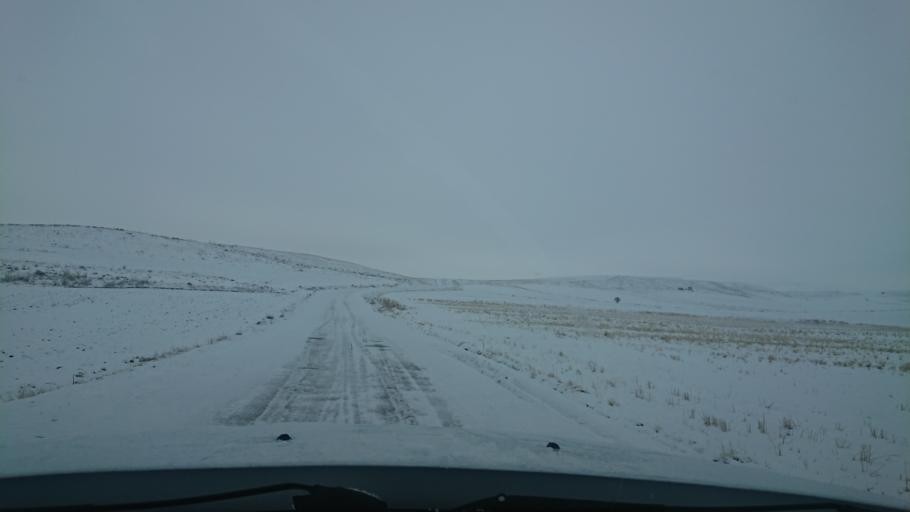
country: TR
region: Aksaray
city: Acipinar
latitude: 38.6849
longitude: 33.8698
